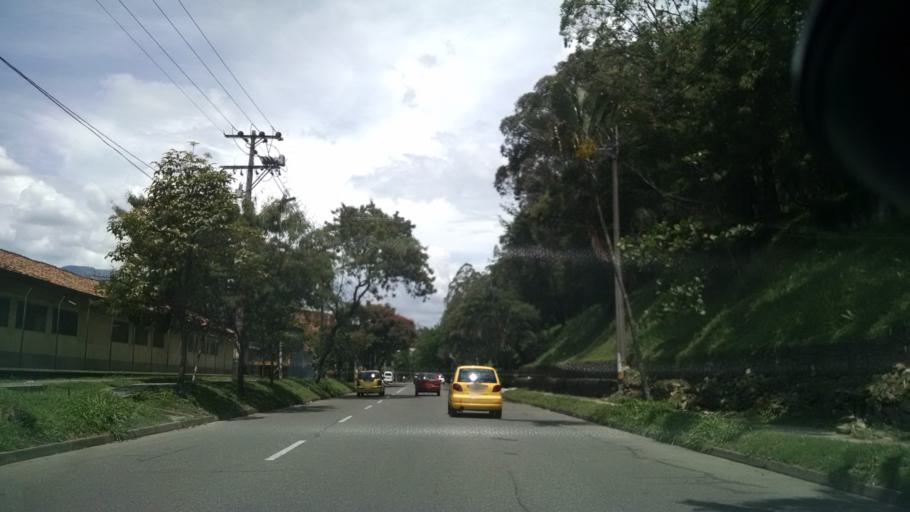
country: CO
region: Antioquia
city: Medellin
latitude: 6.2349
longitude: -75.5827
